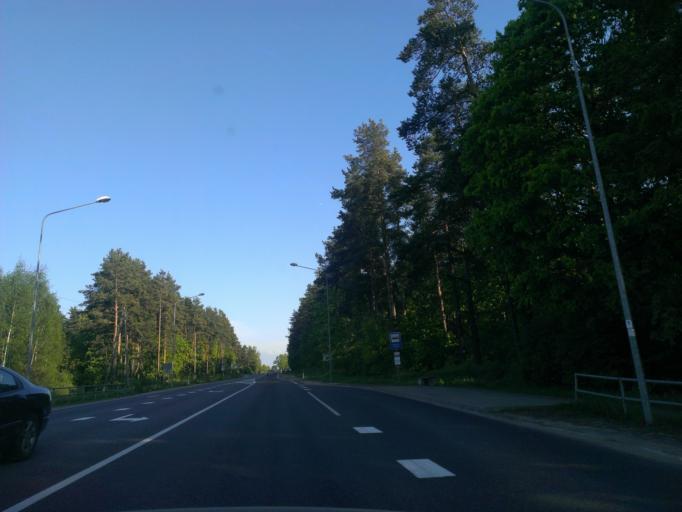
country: LV
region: Kekava
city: Balozi
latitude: 56.8847
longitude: 24.1551
